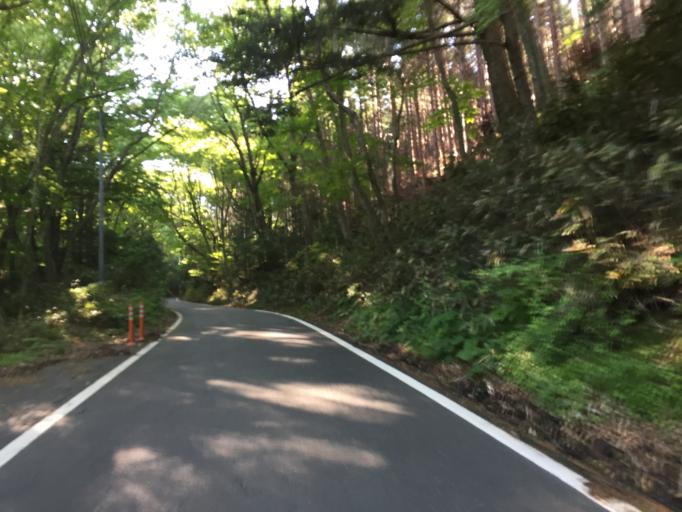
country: JP
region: Ibaraki
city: Kitaibaraki
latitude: 36.9002
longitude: 140.6195
